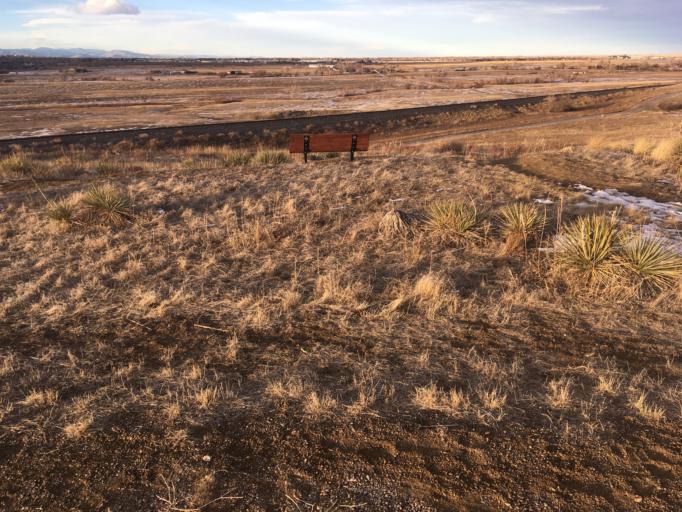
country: US
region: Colorado
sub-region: Broomfield County
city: Broomfield
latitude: 39.9331
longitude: -105.1107
